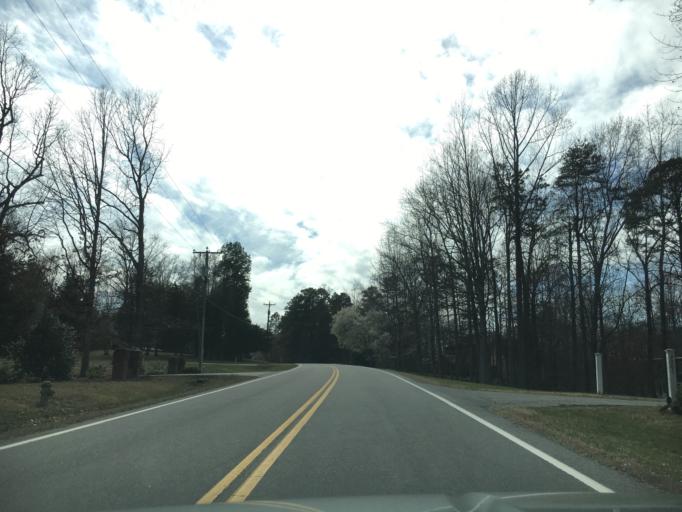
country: US
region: Virginia
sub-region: Halifax County
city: Halifax
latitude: 36.7574
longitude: -78.9135
